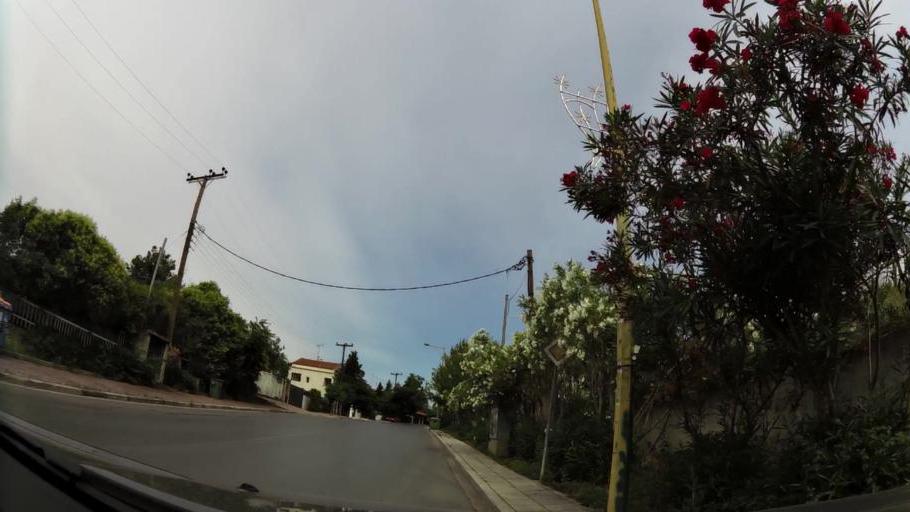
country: GR
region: Central Macedonia
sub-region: Nomos Thessalonikis
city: Panorama
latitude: 40.5870
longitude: 23.0207
